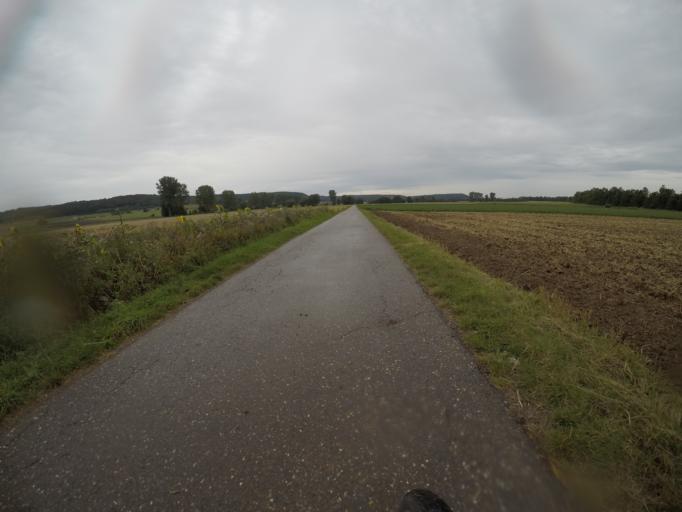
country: DE
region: Baden-Wuerttemberg
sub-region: Regierungsbezirk Stuttgart
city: Ehningen
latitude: 48.6388
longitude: 8.9311
